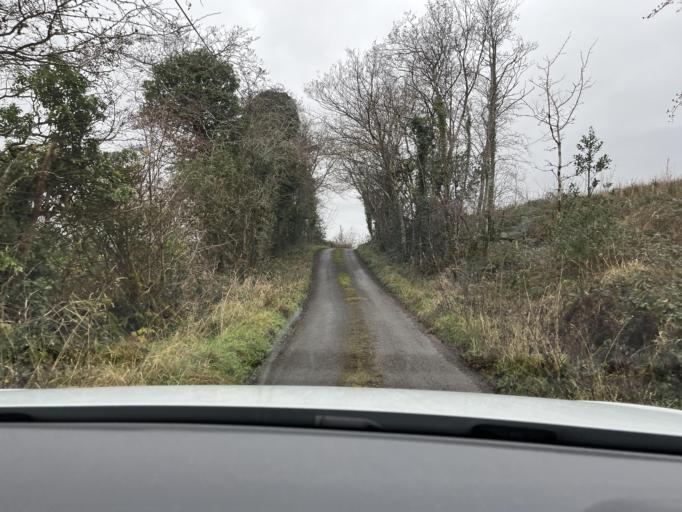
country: IE
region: Connaught
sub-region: County Leitrim
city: Manorhamilton
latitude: 54.2852
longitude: -8.1182
